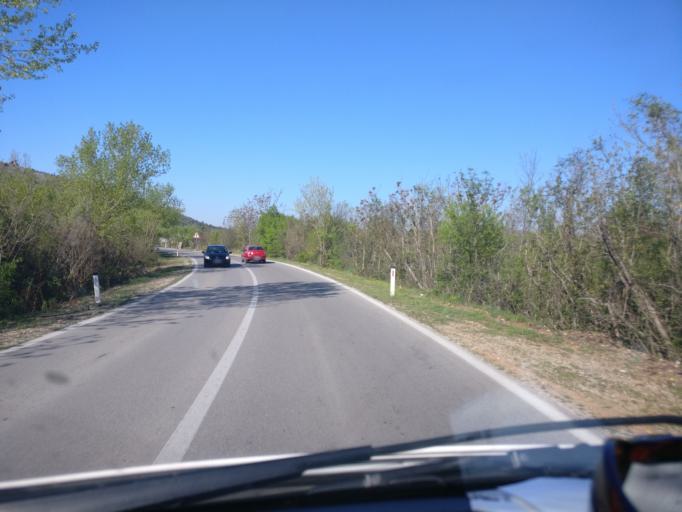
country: BA
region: Federation of Bosnia and Herzegovina
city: Tasovcici
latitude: 43.1214
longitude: 17.7461
